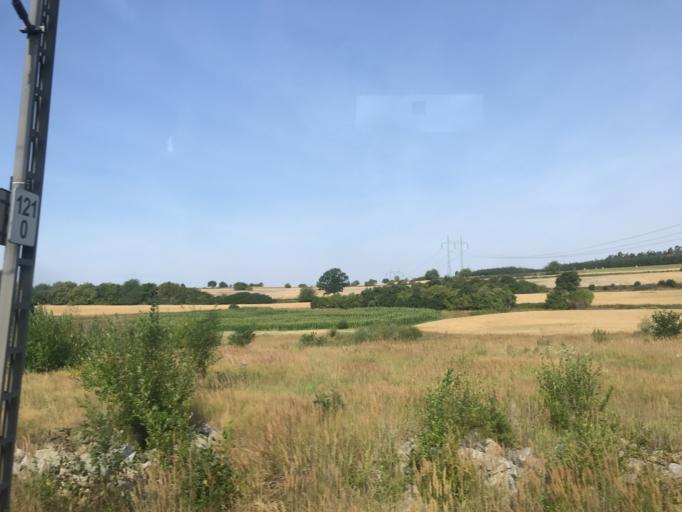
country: CZ
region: Central Bohemia
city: Votice
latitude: 49.6804
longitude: 14.6285
